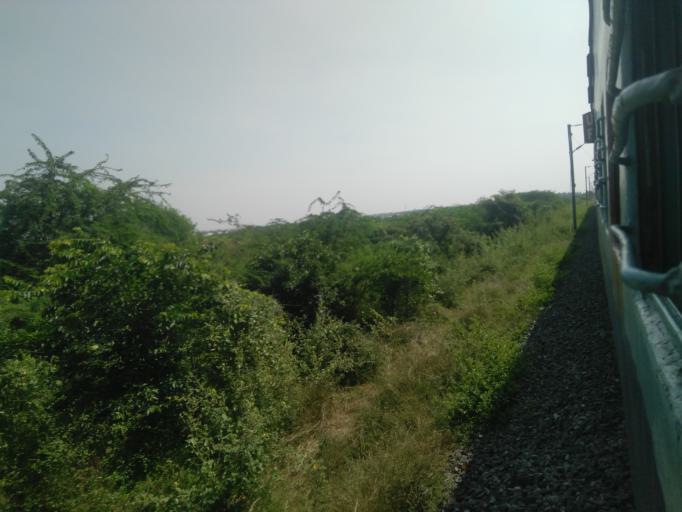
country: IN
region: Tamil Nadu
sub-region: Coimbatore
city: Periyanayakkanpalaiyam
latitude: 11.1287
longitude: 76.9486
